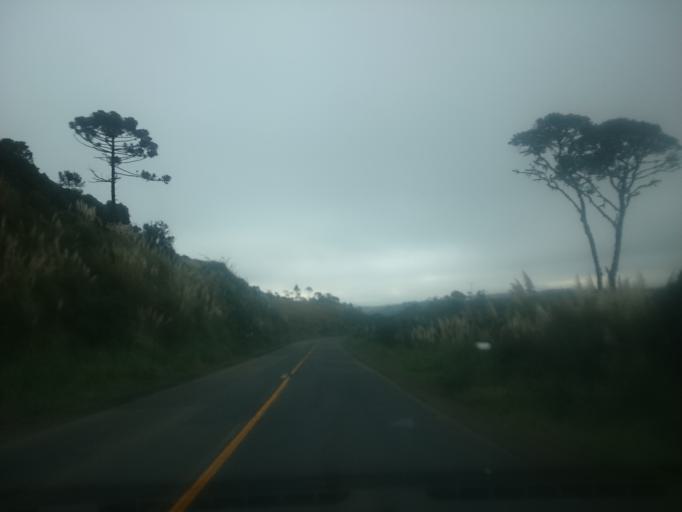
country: BR
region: Santa Catarina
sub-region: Lauro Muller
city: Lauro Muller
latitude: -28.3791
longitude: -49.5582
